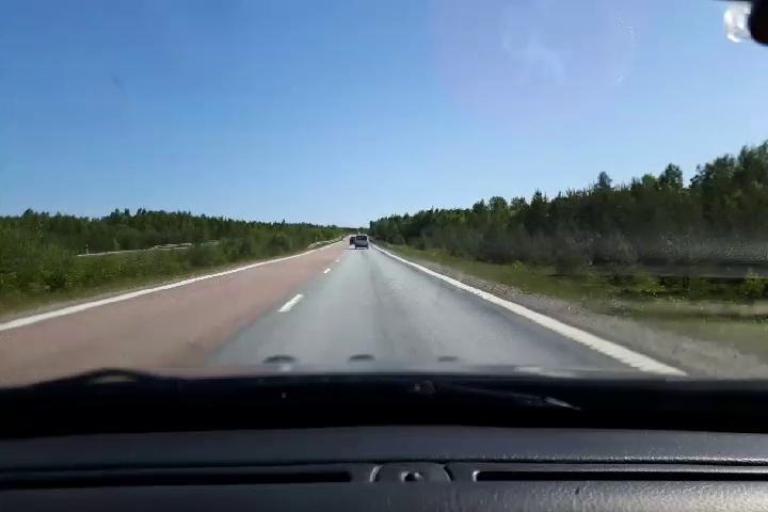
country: SE
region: Gaevleborg
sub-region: Hudiksvalls Kommun
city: Iggesund
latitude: 61.4817
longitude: 16.9858
